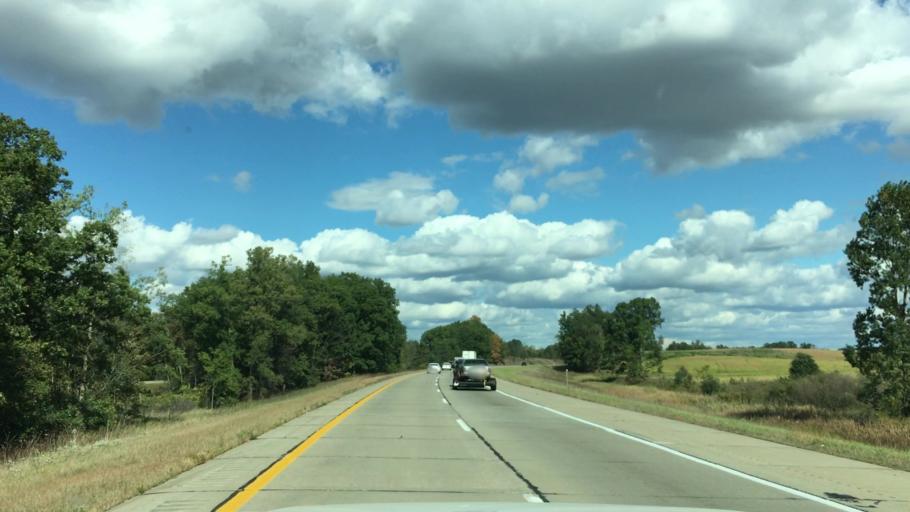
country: US
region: Michigan
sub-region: Eaton County
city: Olivet
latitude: 42.4527
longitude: -84.9446
